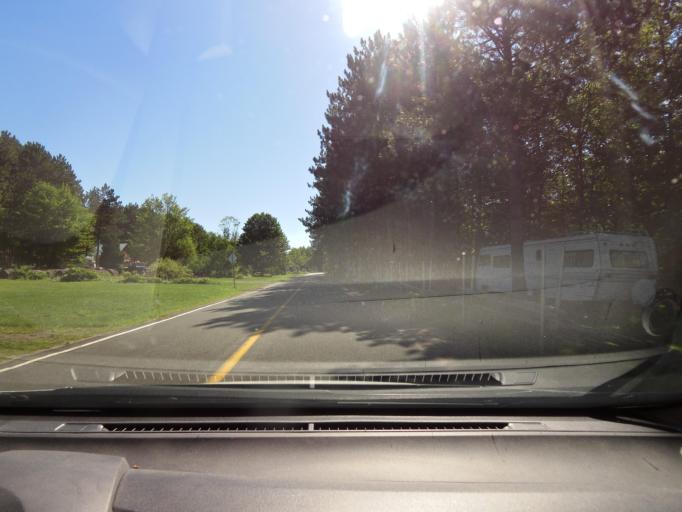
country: CA
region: Quebec
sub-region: Mauricie
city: Becancour
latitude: 46.5515
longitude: -72.4253
